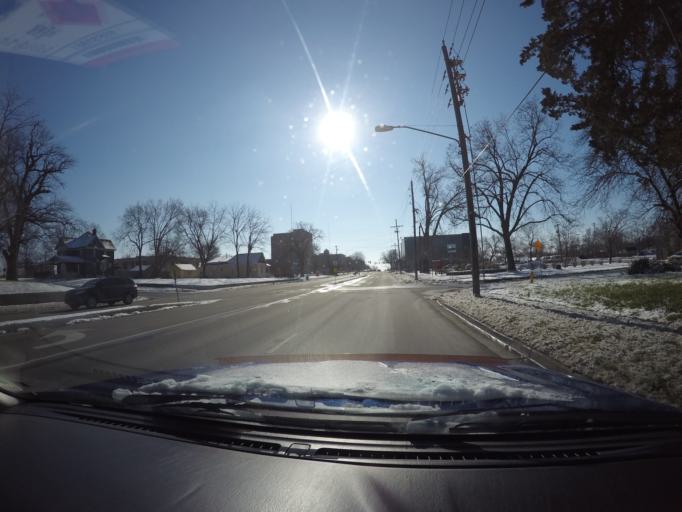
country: US
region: Kansas
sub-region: Johnson County
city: Olathe
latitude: 38.8853
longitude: -94.8208
